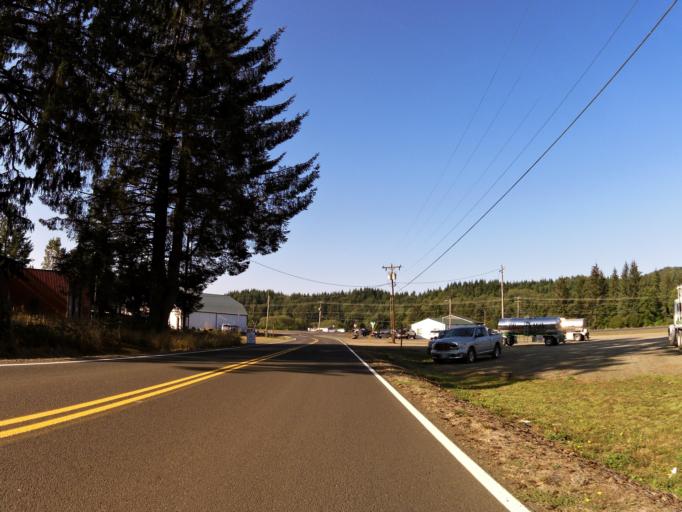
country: US
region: Oregon
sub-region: Tillamook County
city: Tillamook
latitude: 45.3839
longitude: -123.8024
